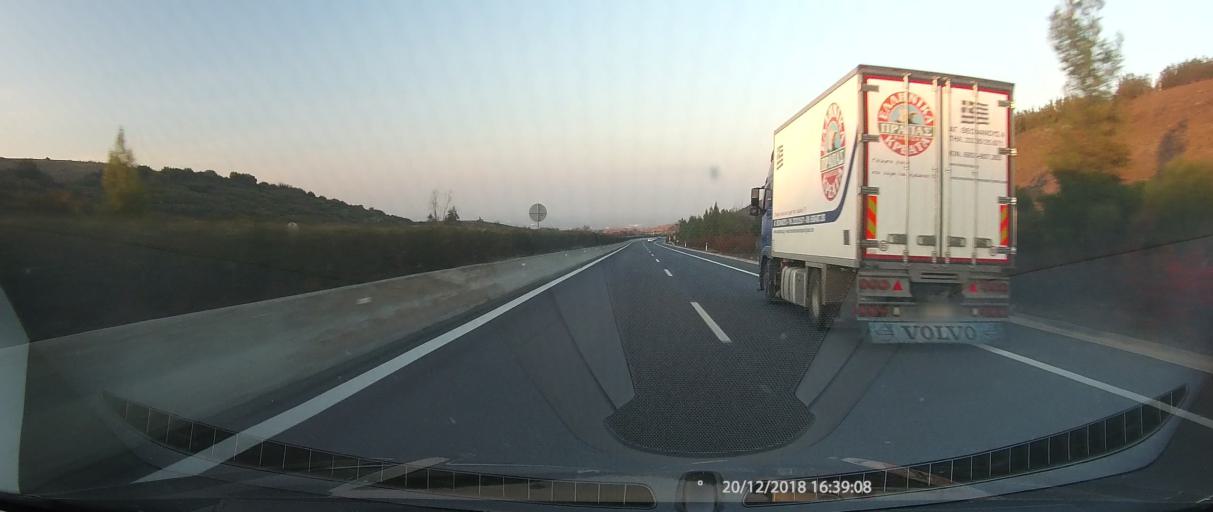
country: GR
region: Thessaly
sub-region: Nomos Magnisias
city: Velestino
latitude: 39.3528
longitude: 22.7726
